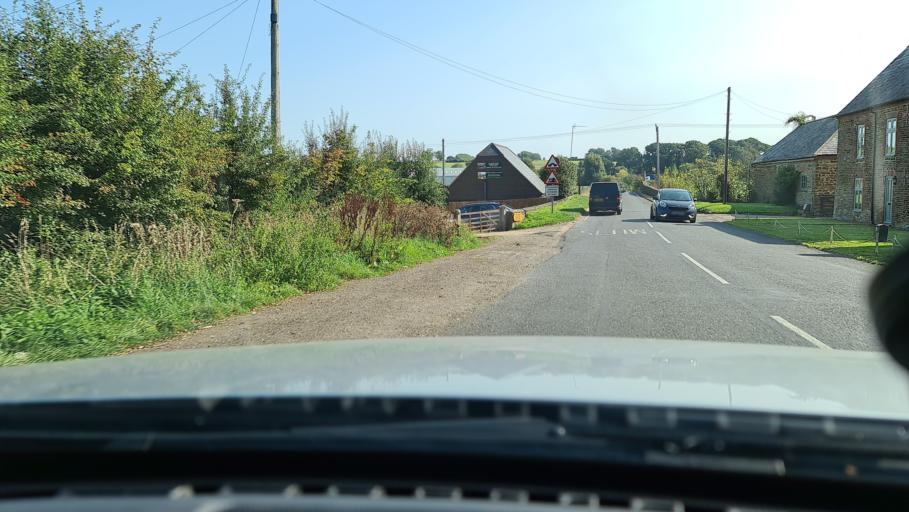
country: GB
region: England
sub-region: Oxfordshire
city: Adderbury
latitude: 52.0312
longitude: -1.2975
